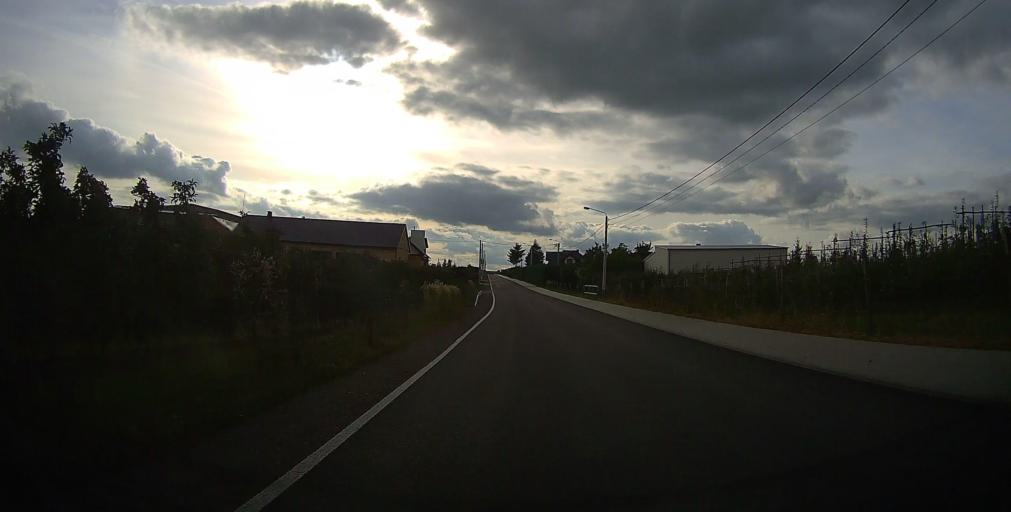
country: PL
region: Masovian Voivodeship
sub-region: Powiat bialobrzeski
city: Promna
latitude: 51.7084
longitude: 20.9362
